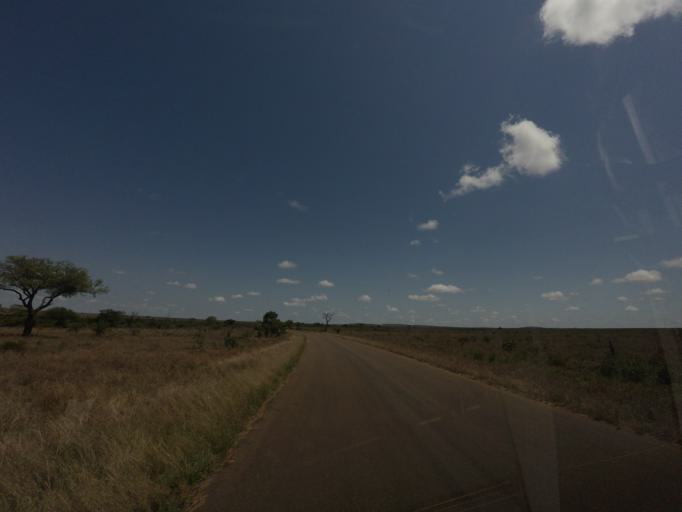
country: ZA
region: Mpumalanga
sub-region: Ehlanzeni District
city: Komatipoort
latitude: -24.9503
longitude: 31.9219
